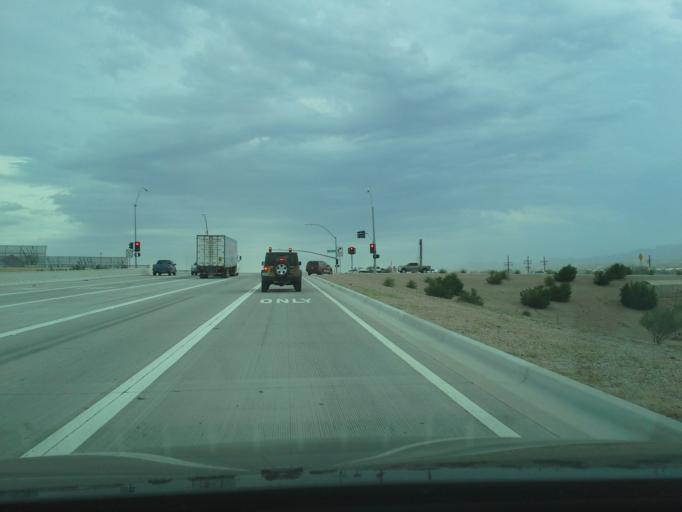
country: US
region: Arizona
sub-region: Pima County
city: Tortolita
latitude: 32.3795
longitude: -111.1110
